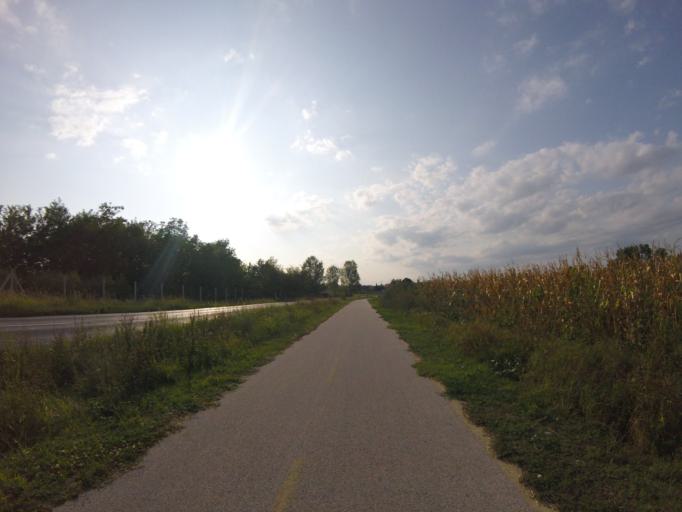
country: HU
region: Gyor-Moson-Sopron
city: Fertod
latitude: 47.6194
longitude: 16.8048
